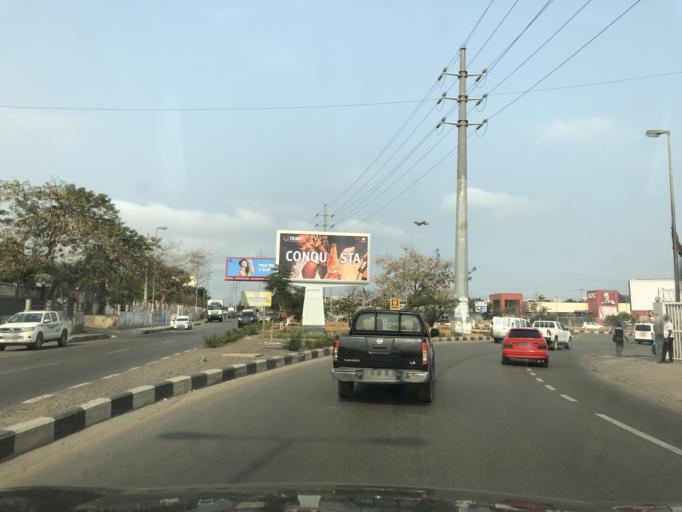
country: AO
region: Luanda
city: Luanda
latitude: -8.8942
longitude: 13.1826
